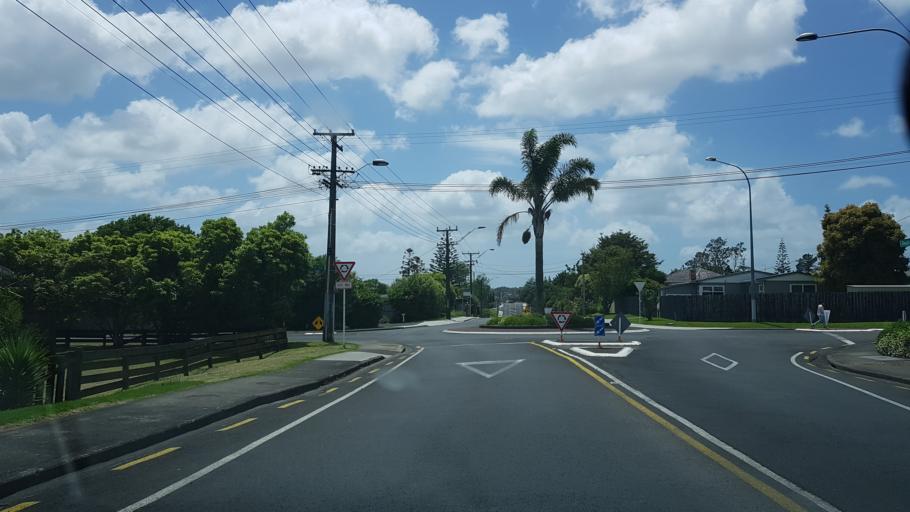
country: NZ
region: Auckland
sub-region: Auckland
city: North Shore
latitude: -36.7893
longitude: 174.6947
